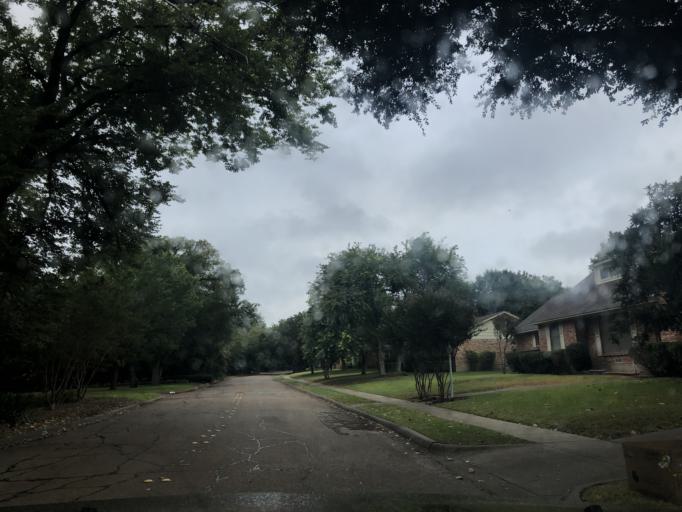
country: US
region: Texas
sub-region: Dallas County
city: Garland
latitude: 32.8724
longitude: -96.6385
